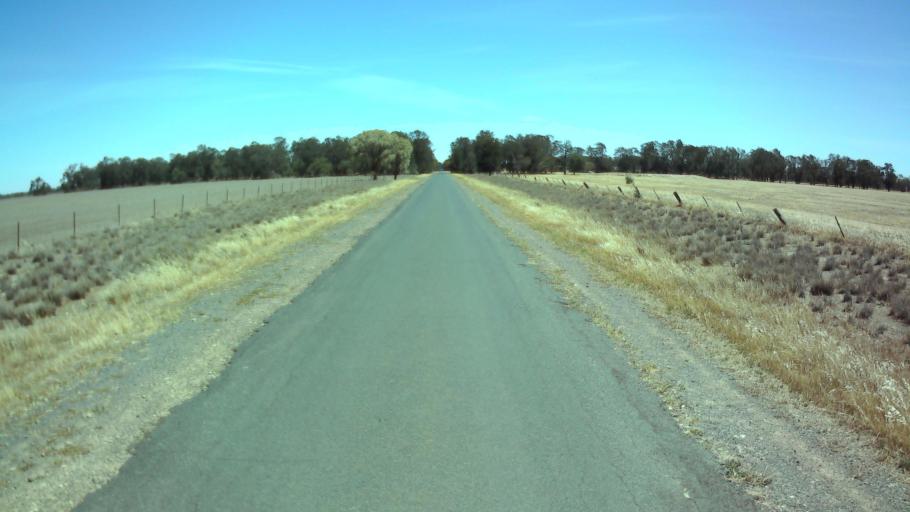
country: AU
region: New South Wales
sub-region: Weddin
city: Grenfell
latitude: -33.8651
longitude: 147.6930
